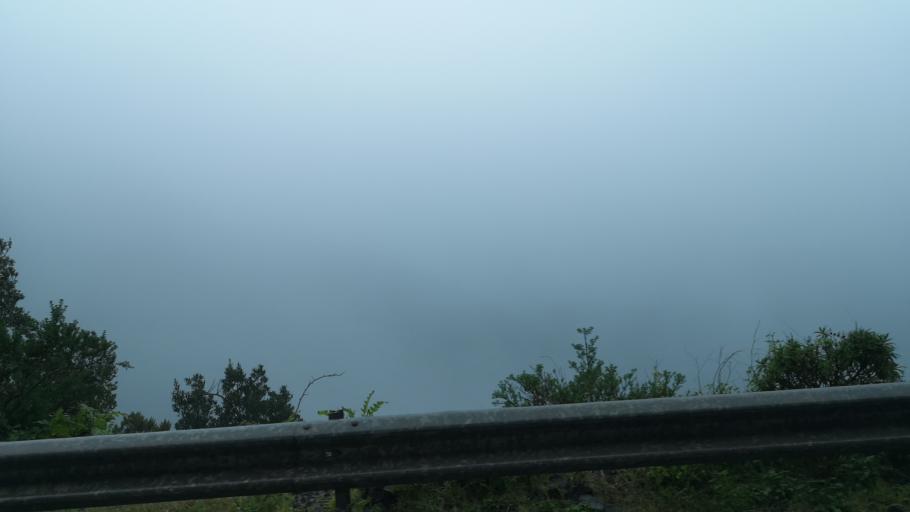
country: ES
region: Canary Islands
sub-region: Provincia de Santa Cruz de Tenerife
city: Hermigua
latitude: 28.1249
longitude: -17.2088
